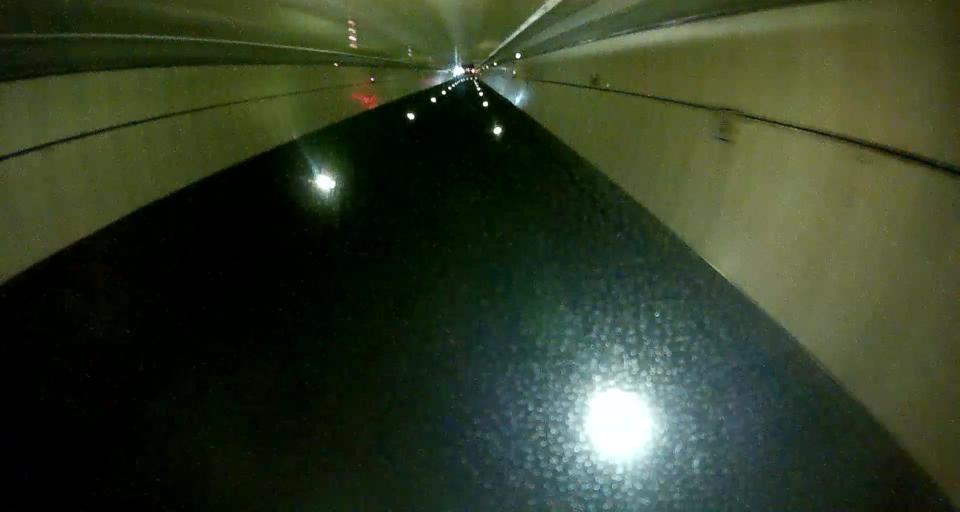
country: JP
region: Iwate
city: Ofunato
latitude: 39.1226
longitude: 141.7789
